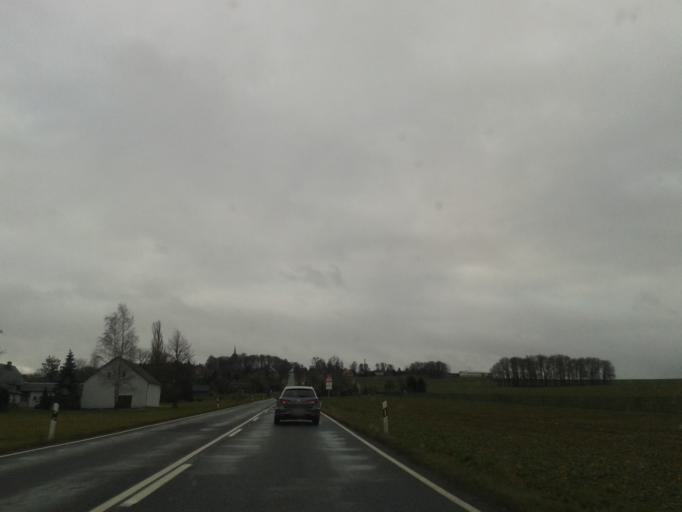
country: DE
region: Saxony
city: Durrhennersdorf
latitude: 51.0420
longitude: 14.6328
